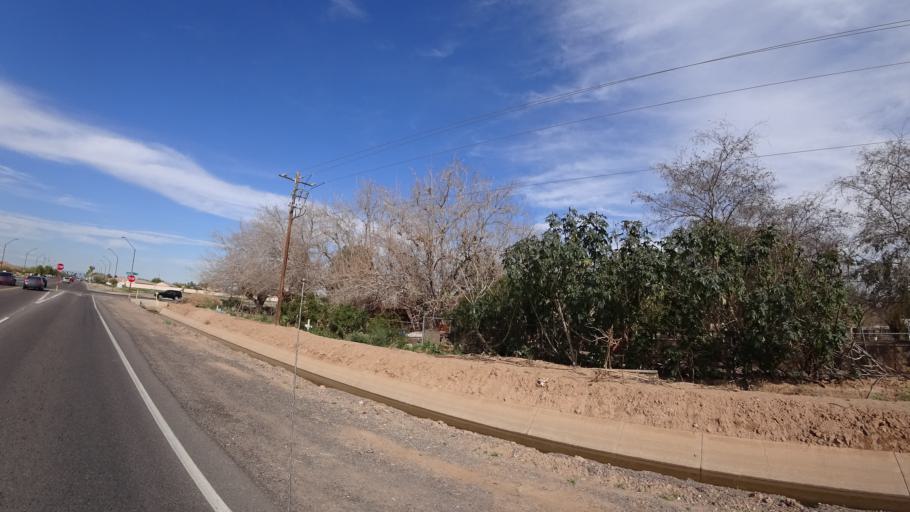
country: US
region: Arizona
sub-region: Maricopa County
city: Avondale
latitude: 33.4199
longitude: -112.3062
